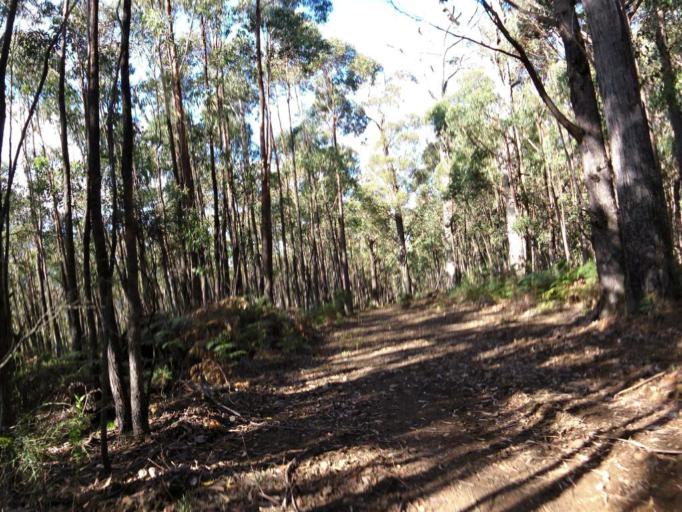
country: AU
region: Victoria
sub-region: Yarra Ranges
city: Millgrove
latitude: -37.7621
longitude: 145.6704
